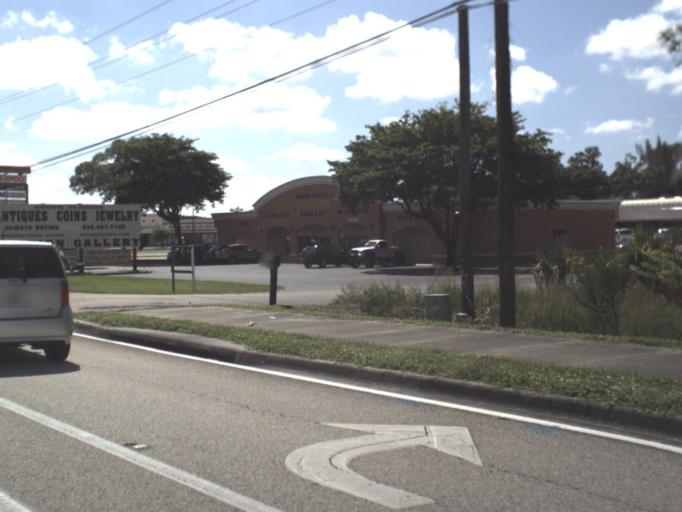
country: US
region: Florida
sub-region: Lee County
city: Villas
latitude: 26.5049
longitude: -81.8582
